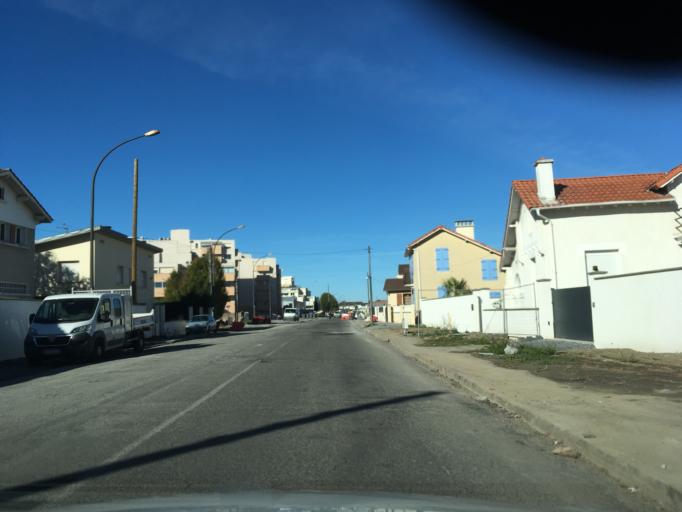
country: FR
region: Aquitaine
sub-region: Departement des Pyrenees-Atlantiques
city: Pau
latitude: 43.3196
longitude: -0.3488
